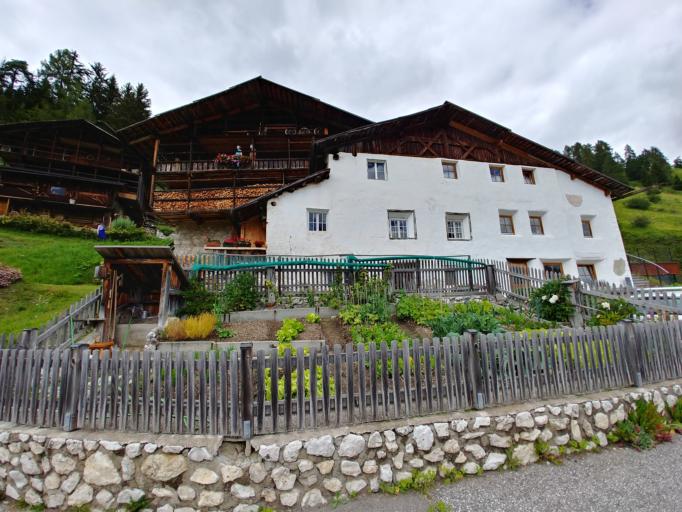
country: IT
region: Trentino-Alto Adige
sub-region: Bolzano
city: Santa Cristina Valgardena
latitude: 46.5639
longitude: 11.7279
